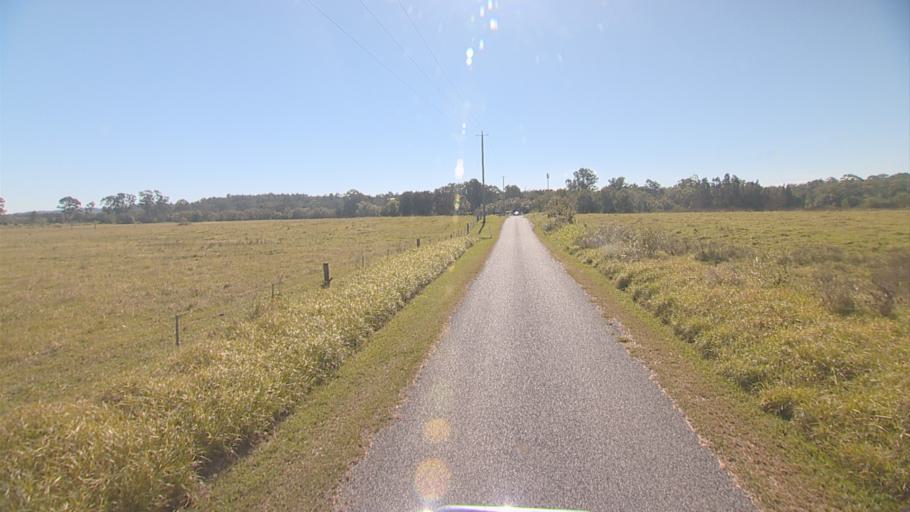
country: AU
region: Queensland
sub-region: Gold Coast
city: Yatala
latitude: -27.6831
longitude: 153.2251
